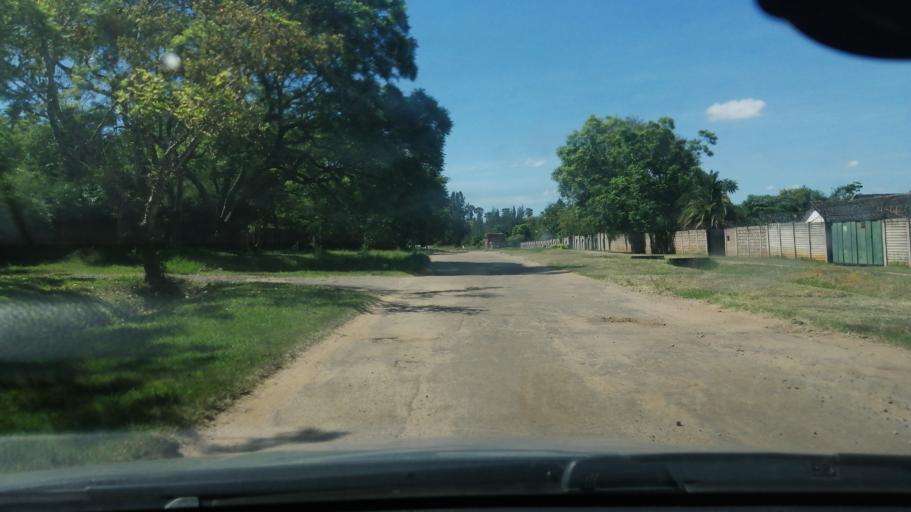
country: ZW
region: Harare
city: Harare
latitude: -17.8152
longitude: 31.1287
